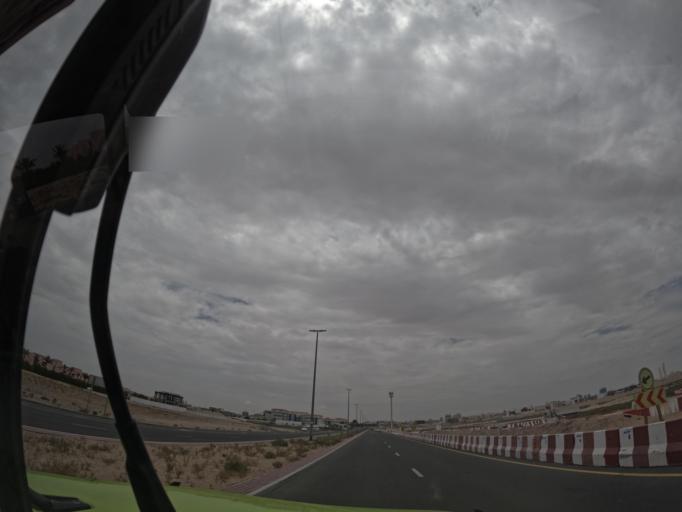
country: AE
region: Ash Shariqah
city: Sharjah
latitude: 25.1569
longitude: 55.3718
